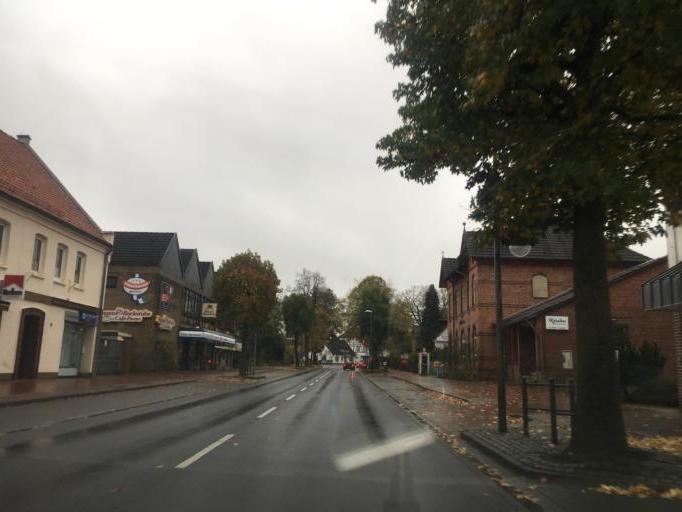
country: DE
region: Lower Saxony
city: Bergen
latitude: 52.8078
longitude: 9.9650
